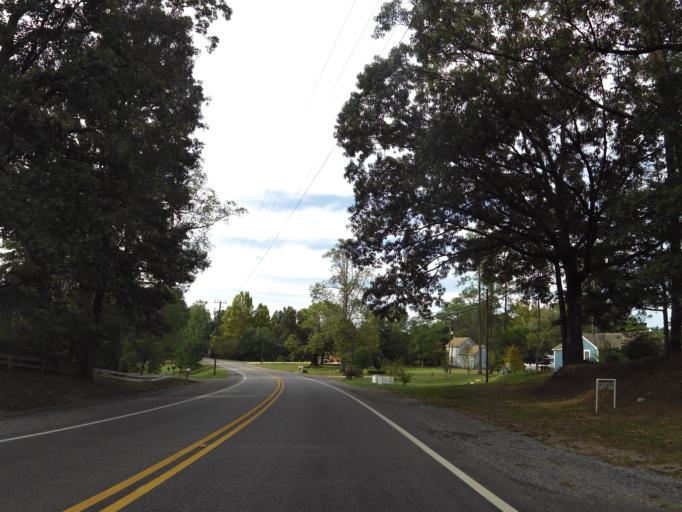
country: US
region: Alabama
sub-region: Monroe County
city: Monroeville
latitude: 31.5378
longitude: -87.3242
